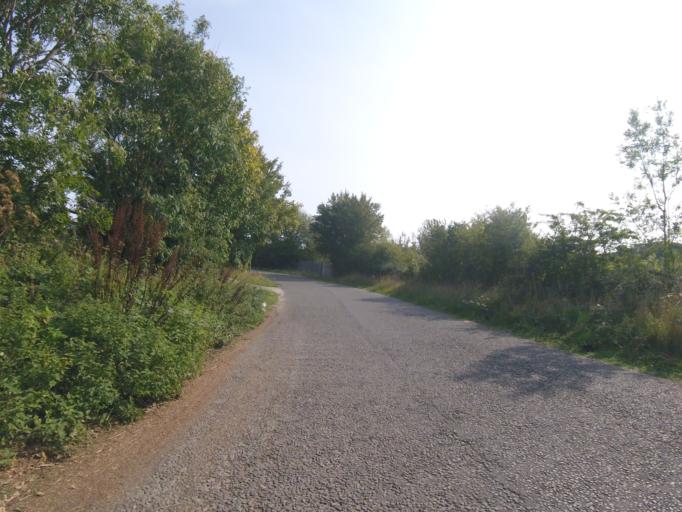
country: GB
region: England
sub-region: Brighton and Hove
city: Hove
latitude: 50.8694
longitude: -0.1564
